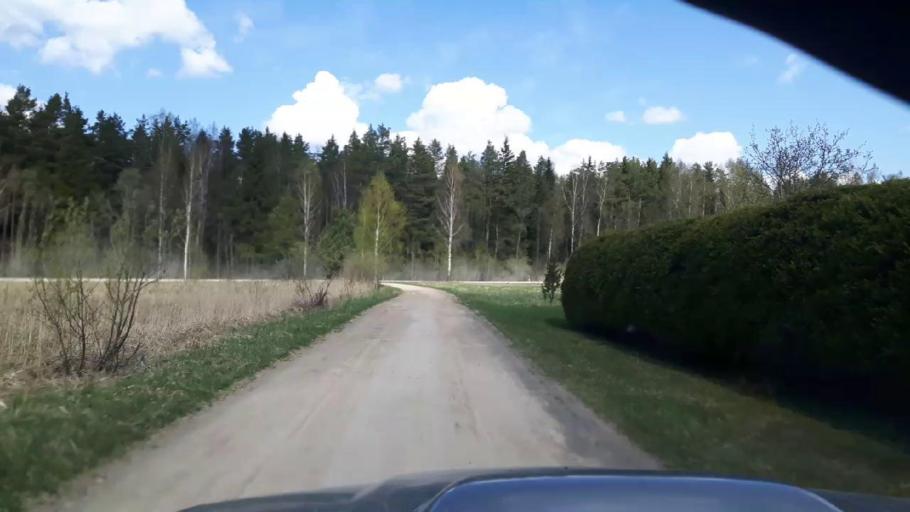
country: EE
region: Paernumaa
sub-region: Tootsi vald
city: Tootsi
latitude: 58.5024
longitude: 24.9296
